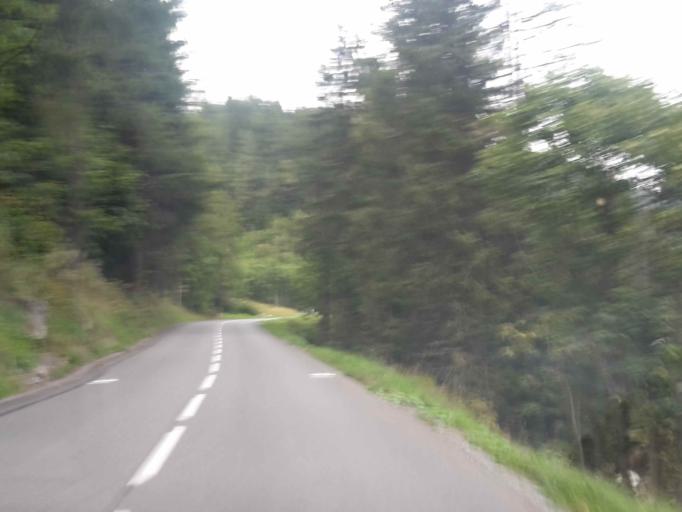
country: FR
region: Rhone-Alpes
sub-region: Departement de la Haute-Savoie
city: Chamonix-Mont-Blanc
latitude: 45.9890
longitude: 6.9287
